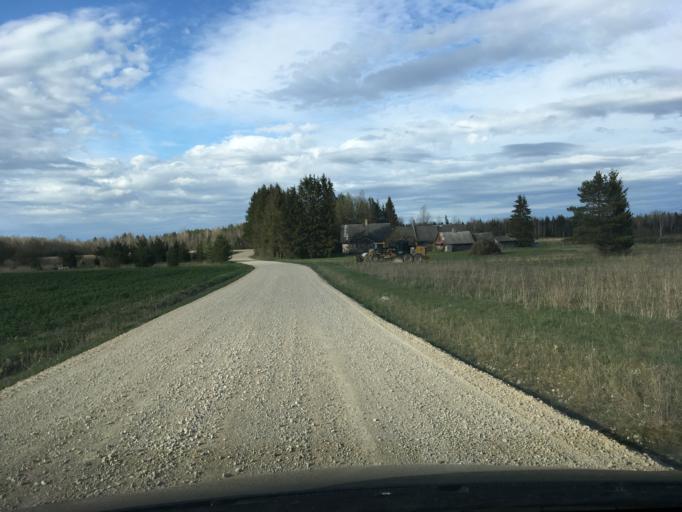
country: EE
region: Raplamaa
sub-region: Maerjamaa vald
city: Marjamaa
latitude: 58.9794
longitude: 24.3609
